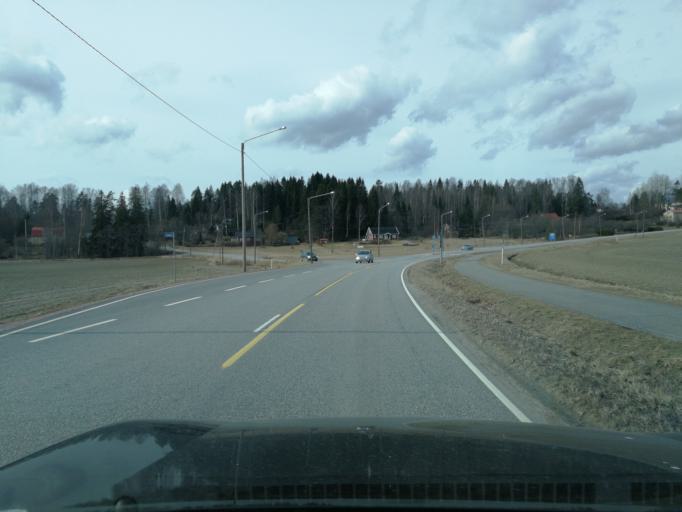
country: FI
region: Uusimaa
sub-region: Helsinki
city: Siuntio
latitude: 60.1637
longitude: 24.1986
